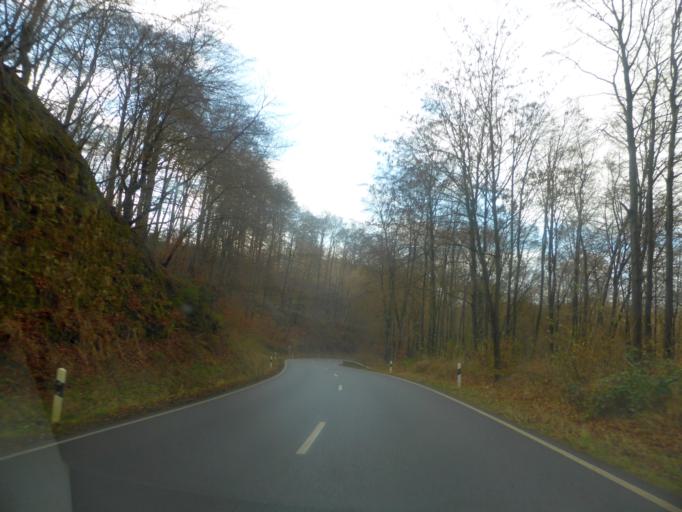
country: LU
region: Luxembourg
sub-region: Canton de Mersch
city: Tuntange
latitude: 49.7212
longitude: 6.0017
